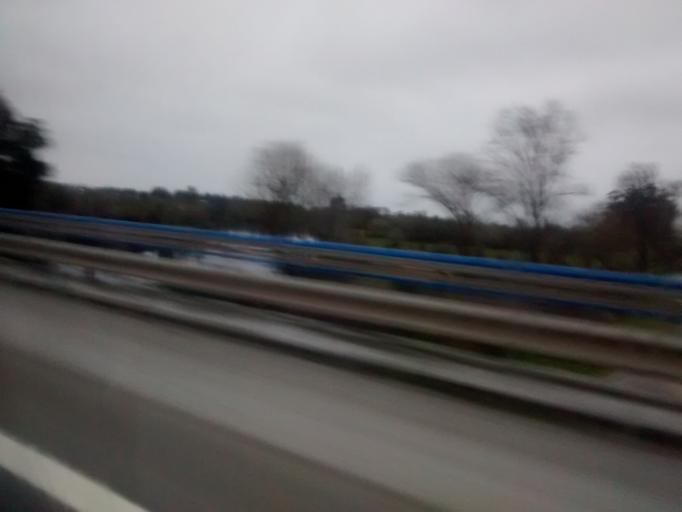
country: PT
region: Aveiro
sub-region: Aveiro
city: Eixo
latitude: 40.6781
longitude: -8.5711
